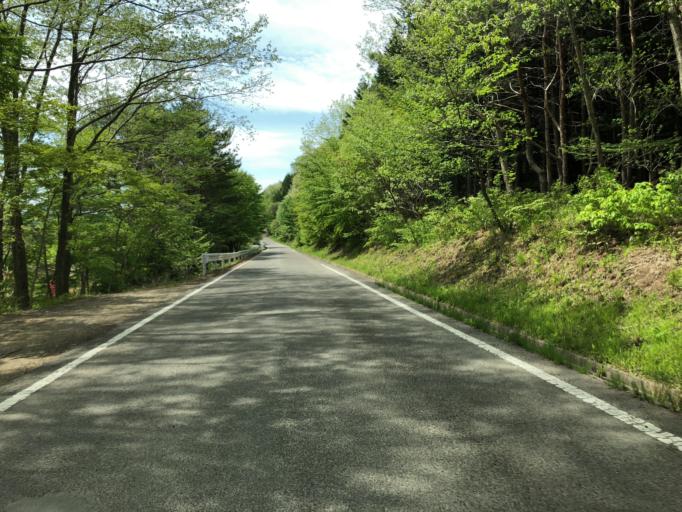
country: JP
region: Fukushima
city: Yanagawamachi-saiwaicho
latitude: 37.7197
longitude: 140.7093
